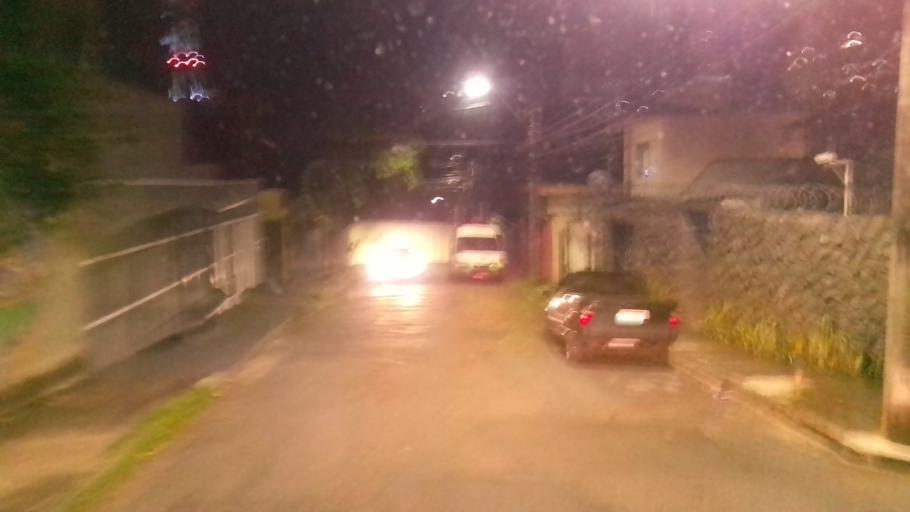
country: BR
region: Minas Gerais
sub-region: Belo Horizonte
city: Belo Horizonte
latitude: -19.9017
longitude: -43.9620
